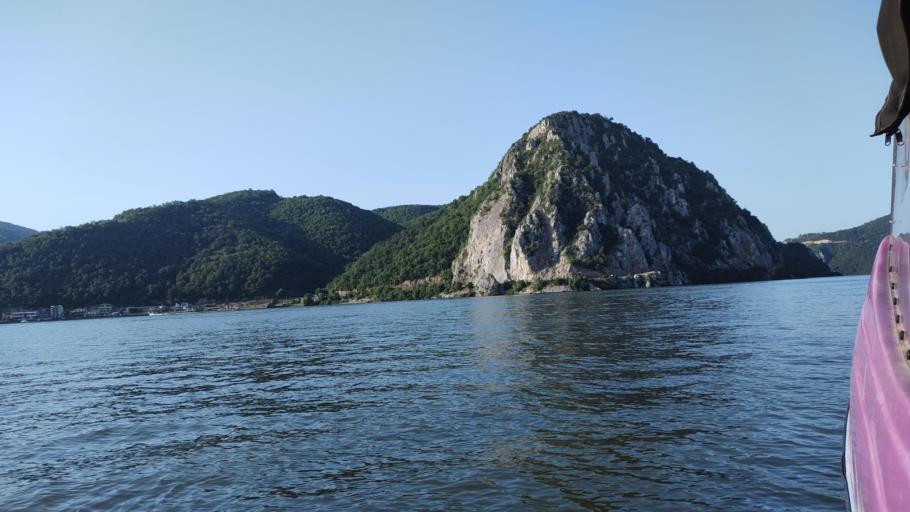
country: RO
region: Mehedinti
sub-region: Comuna Dubova
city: Dubova
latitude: 44.6254
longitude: 22.2774
